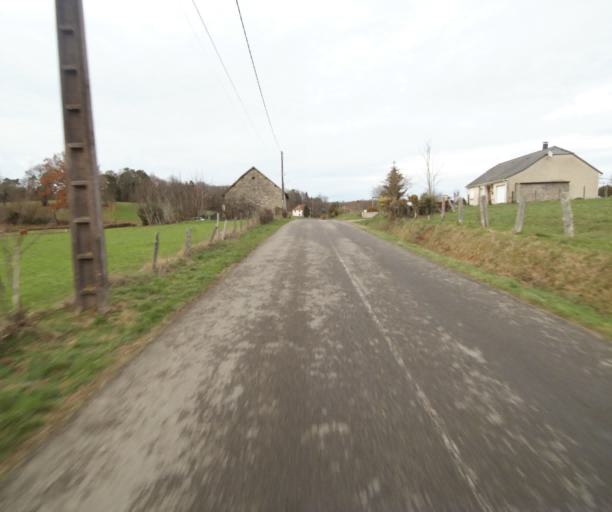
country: FR
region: Limousin
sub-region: Departement de la Correze
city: Chameyrat
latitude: 45.2397
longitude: 1.6998
